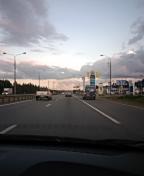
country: RU
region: Moskovskaya
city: Zhukovskiy
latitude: 55.5281
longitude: 38.1107
